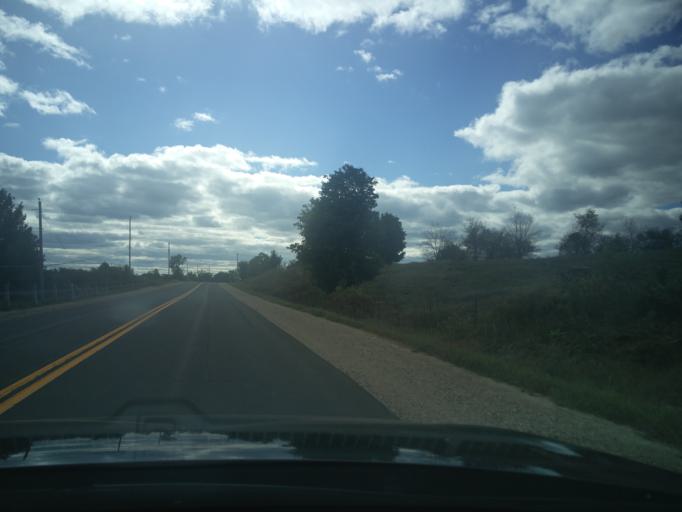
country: CA
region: Ontario
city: Perth
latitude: 44.7881
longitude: -76.3448
